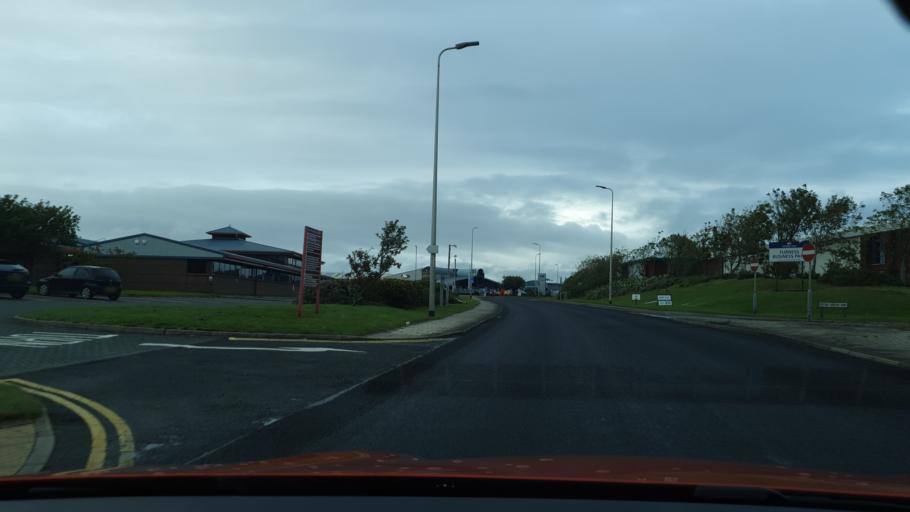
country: GB
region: England
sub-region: Cumbria
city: Barrow in Furness
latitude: 54.1178
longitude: -3.2412
